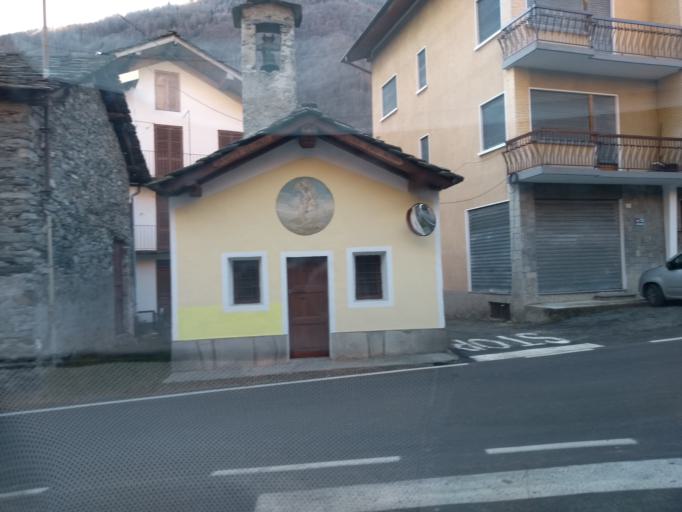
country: IT
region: Piedmont
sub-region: Provincia di Torino
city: Chialamberto
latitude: 45.3581
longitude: 7.3559
